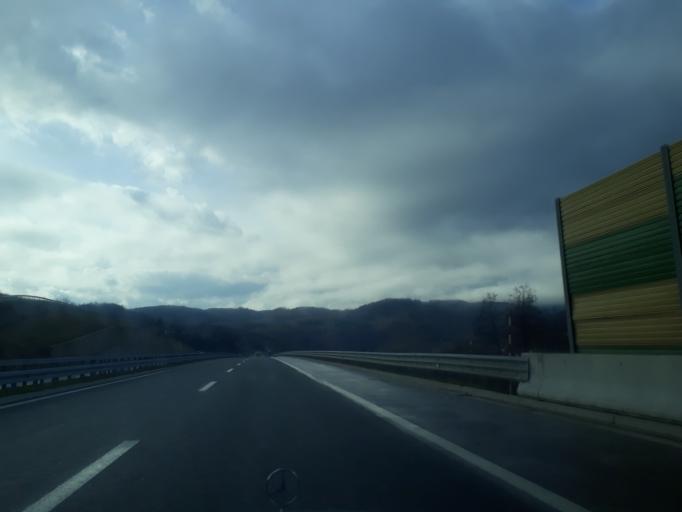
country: BA
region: Federation of Bosnia and Herzegovina
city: Polje
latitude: 43.8485
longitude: 18.1298
